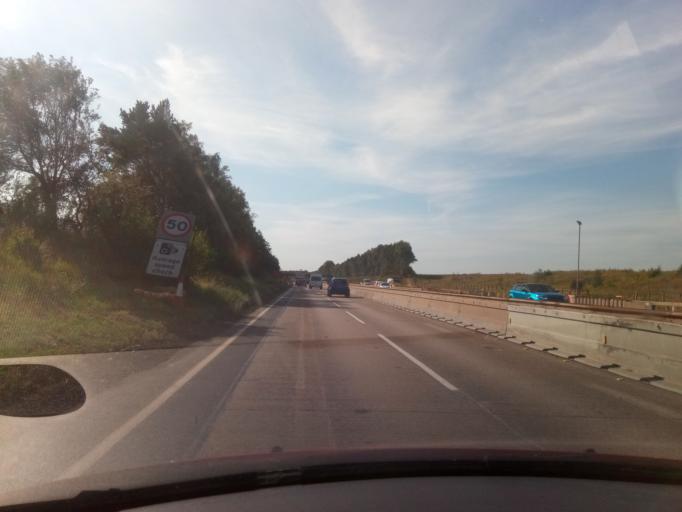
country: GB
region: England
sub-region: Stockton-on-Tees
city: Billingham
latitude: 54.6204
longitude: -1.3158
